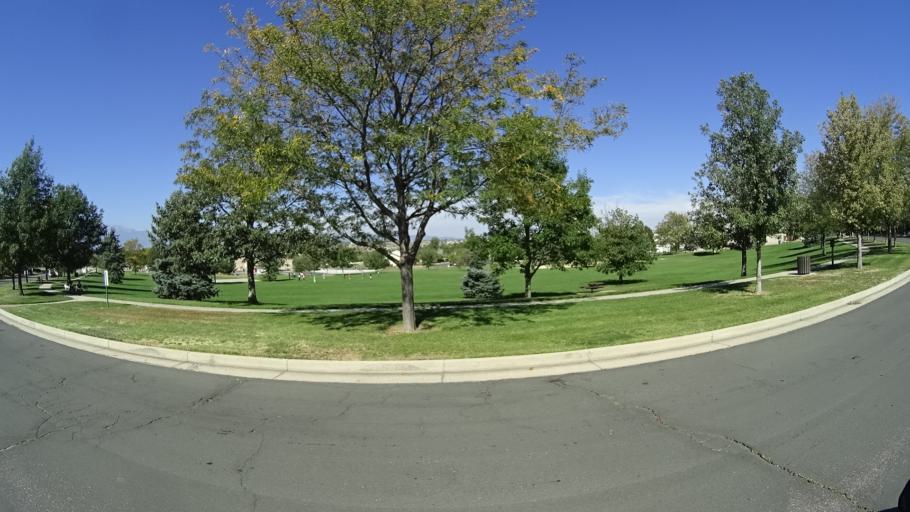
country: US
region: Colorado
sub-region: El Paso County
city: Cimarron Hills
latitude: 38.8777
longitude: -104.6970
